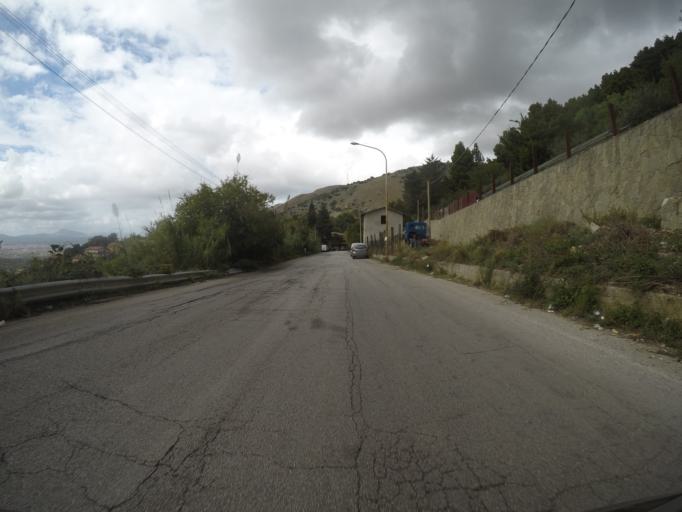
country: IT
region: Sicily
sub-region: Palermo
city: Montelepre
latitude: 38.0938
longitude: 13.1681
